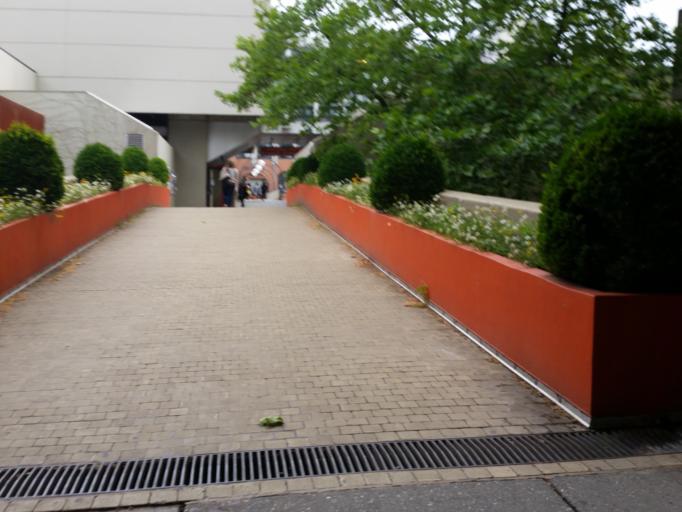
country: BE
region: Flanders
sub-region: Provincie Vlaams-Brabant
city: Kraainem
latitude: 50.8516
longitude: 4.4539
